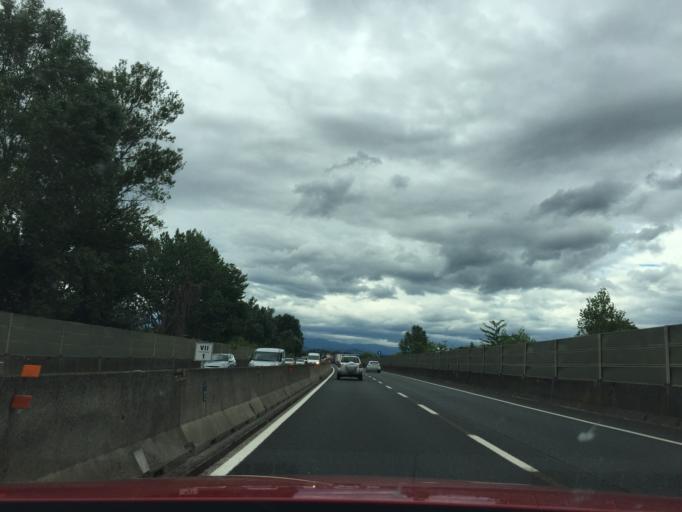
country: IT
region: Tuscany
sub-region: Province of Florence
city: Mantignano-Ugnano
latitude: 43.7708
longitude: 11.1740
